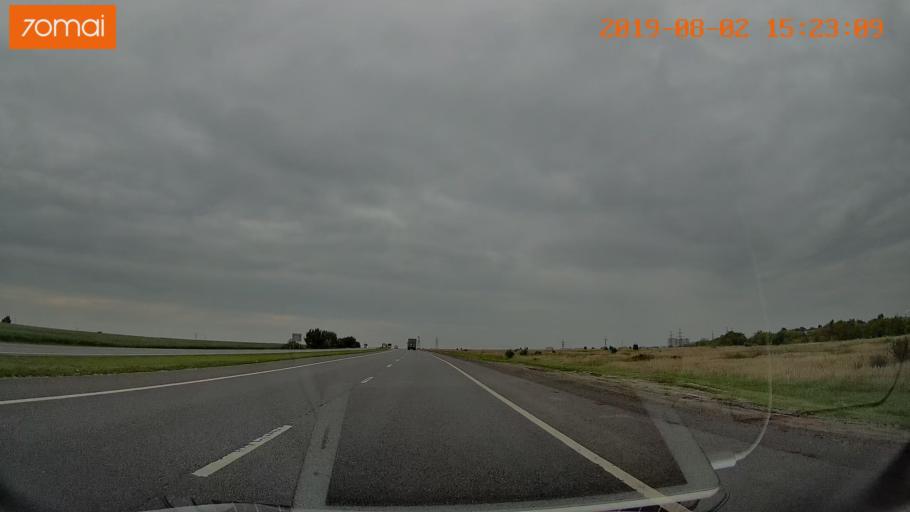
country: RU
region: Moskovskaya
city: Voskresensk
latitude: 55.3122
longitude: 38.6159
